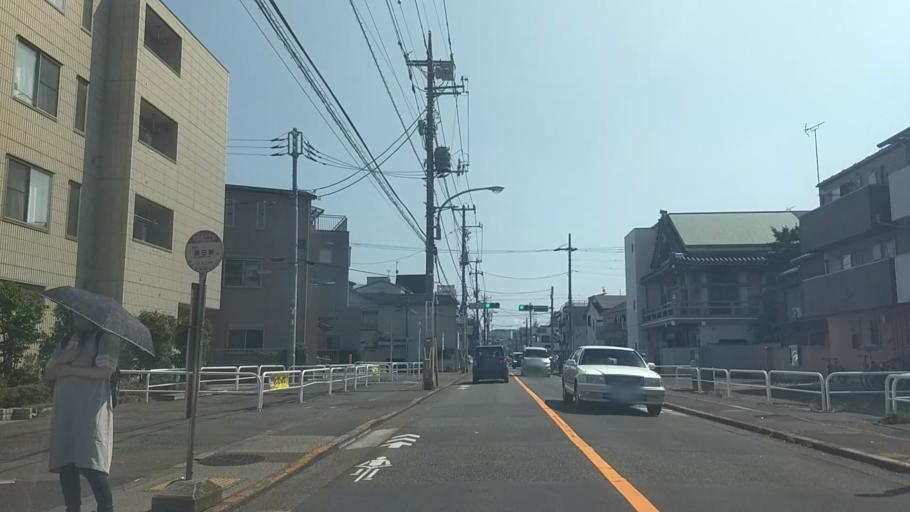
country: JP
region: Kanagawa
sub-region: Kawasaki-shi
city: Kawasaki
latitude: 35.5776
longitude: 139.7271
